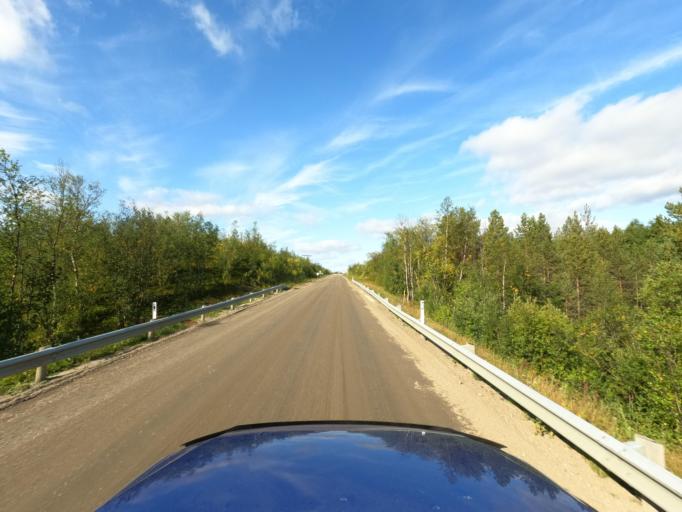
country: NO
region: Finnmark Fylke
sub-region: Porsanger
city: Lakselv
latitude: 69.8775
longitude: 25.0272
